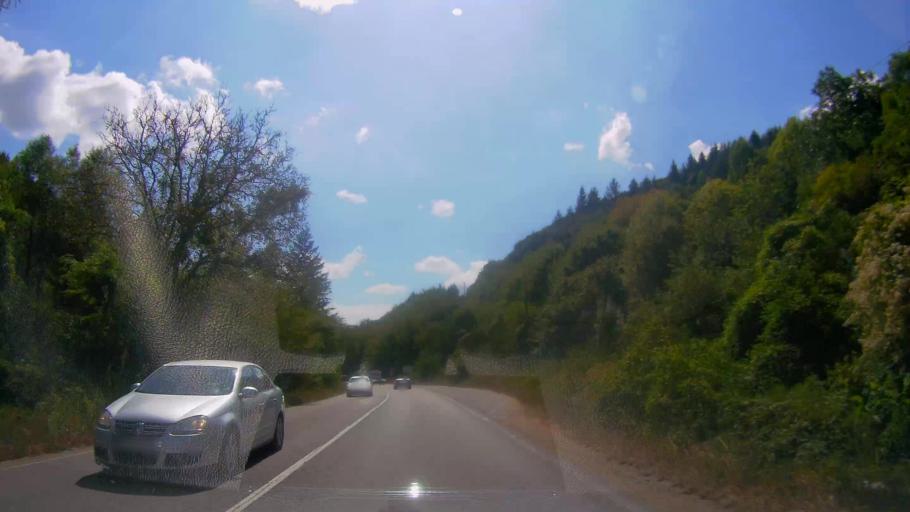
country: BG
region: Stara Zagora
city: Gurkovo
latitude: 42.7468
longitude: 25.7093
